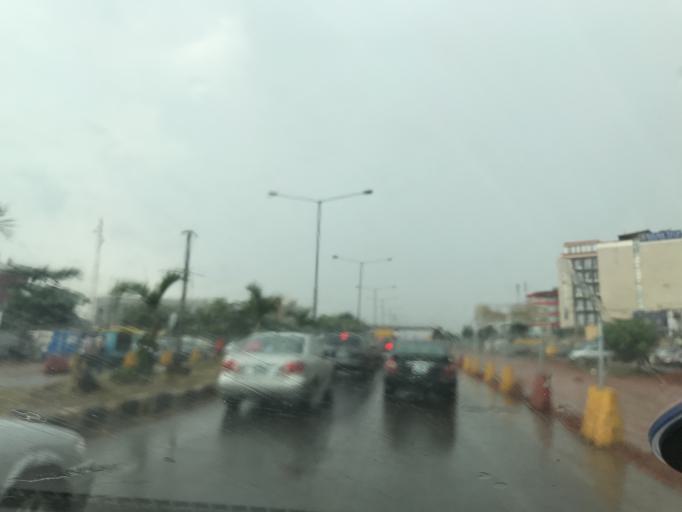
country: NG
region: Lagos
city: Oshodi
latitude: 6.5513
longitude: 3.3311
